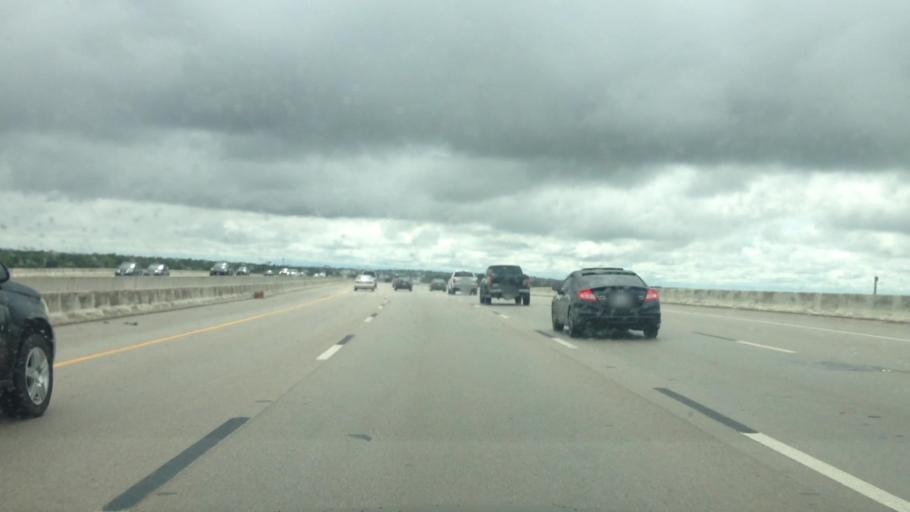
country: US
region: Texas
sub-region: Tarrant County
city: Lake Worth
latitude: 32.7950
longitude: -97.4520
